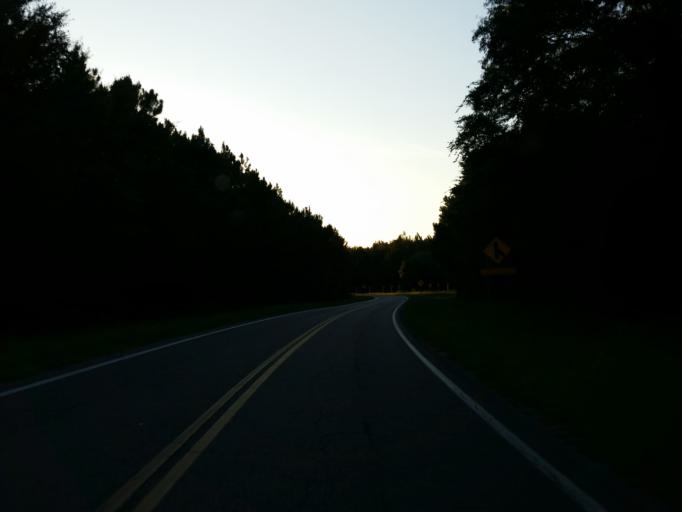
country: US
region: Georgia
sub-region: Berrien County
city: Nashville
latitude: 31.1998
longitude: -83.2275
